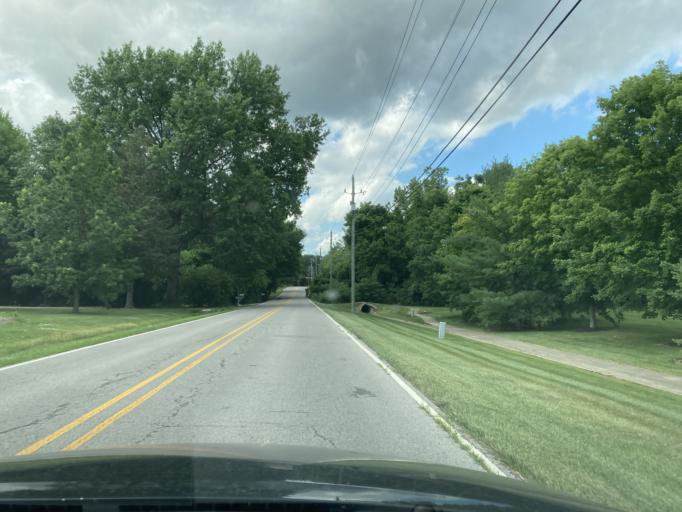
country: US
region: Indiana
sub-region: Marion County
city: Meridian Hills
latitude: 39.8793
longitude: -86.2221
